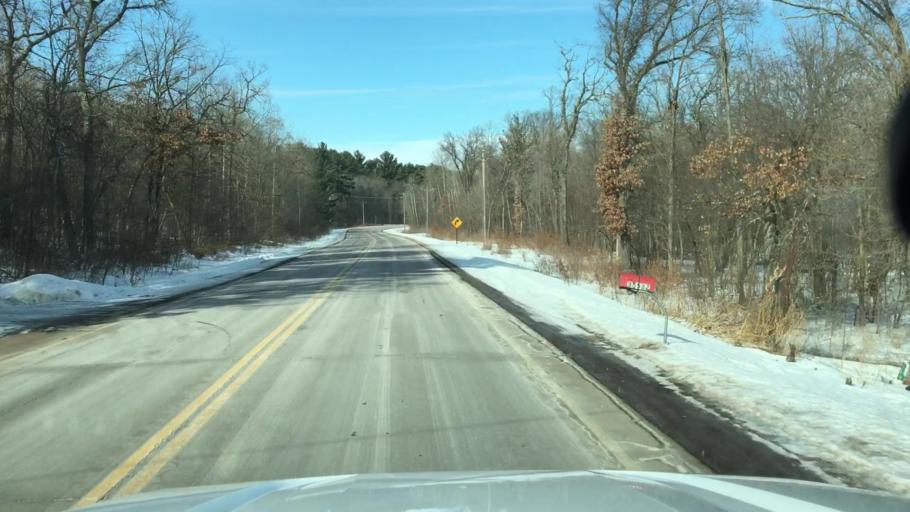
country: US
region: Wisconsin
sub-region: Polk County
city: Saint Croix Falls
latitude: 45.4641
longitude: -92.6834
